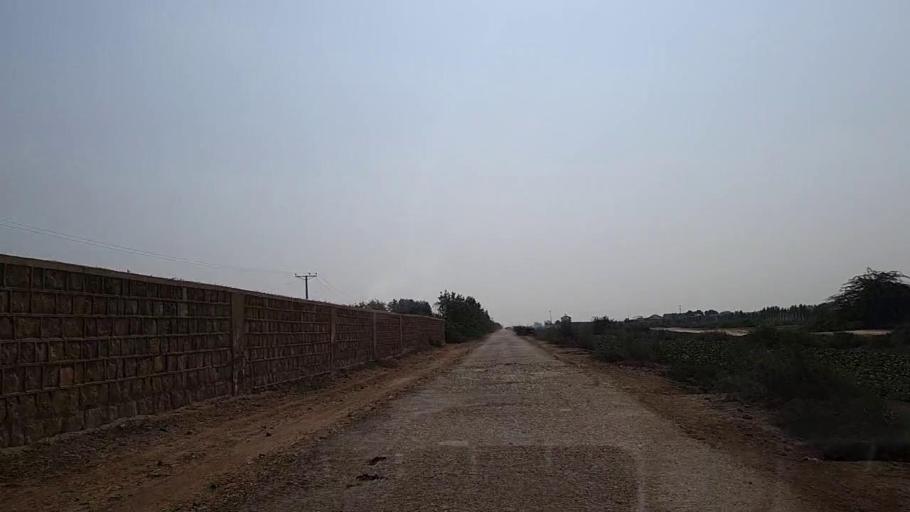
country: PK
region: Sindh
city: Thatta
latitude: 24.7238
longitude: 67.7684
